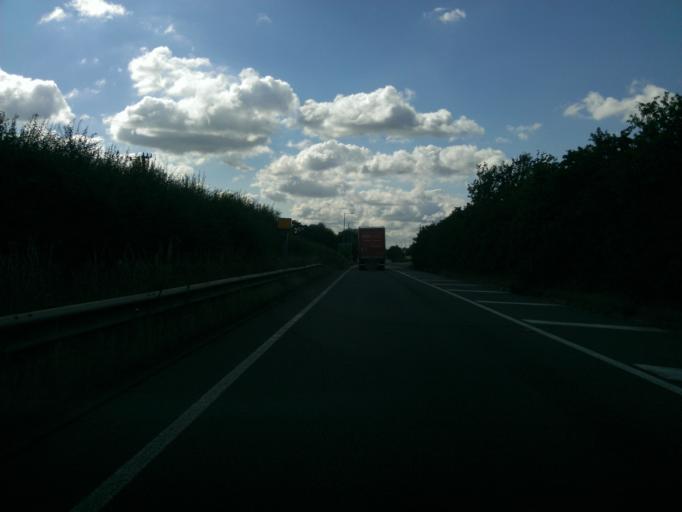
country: GB
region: England
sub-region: Warwickshire
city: Nuneaton
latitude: 52.5562
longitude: -1.4752
